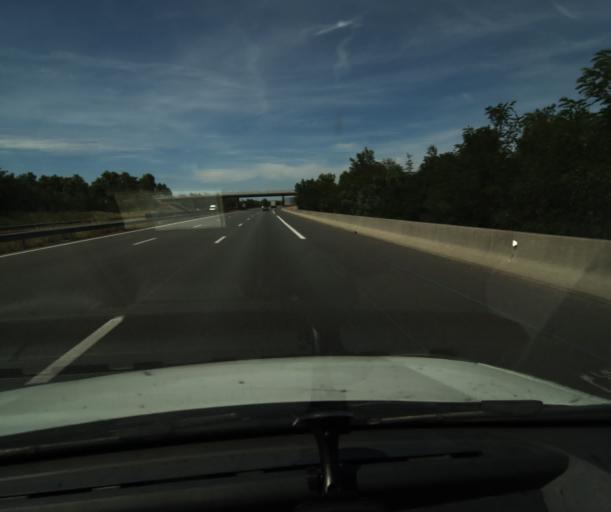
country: FR
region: Midi-Pyrenees
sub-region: Departement du Tarn-et-Garonne
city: Campsas
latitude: 43.8972
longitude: 1.3166
